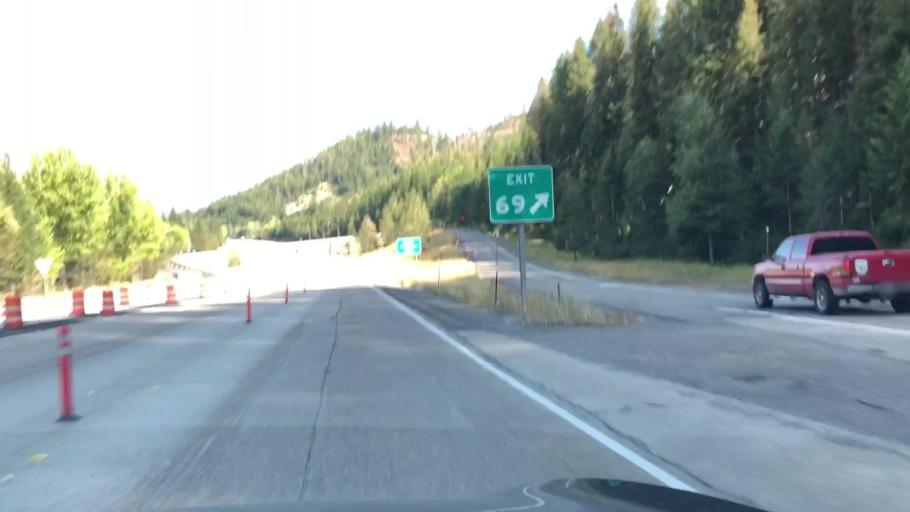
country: US
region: Idaho
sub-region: Shoshone County
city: Wallace
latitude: 47.4686
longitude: -115.7905
